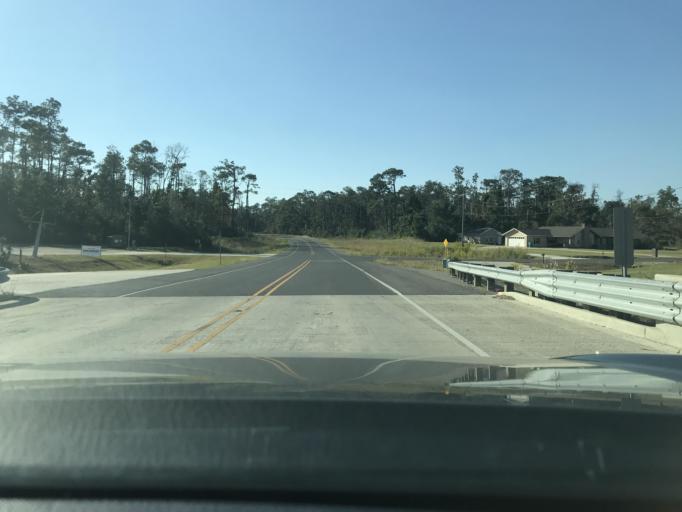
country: US
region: Louisiana
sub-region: Calcasieu Parish
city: Moss Bluff
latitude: 30.3038
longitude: -93.2488
